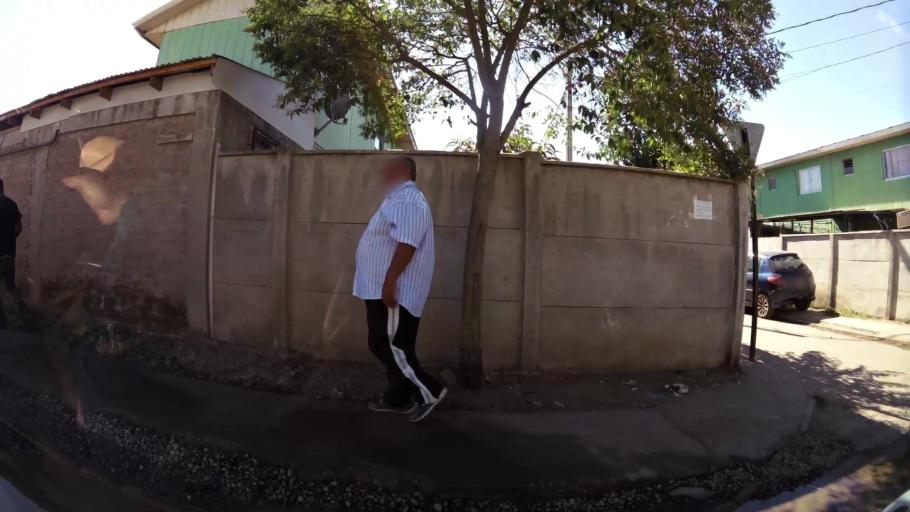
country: CL
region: O'Higgins
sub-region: Provincia de Colchagua
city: Chimbarongo
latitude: -34.5727
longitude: -71.0026
